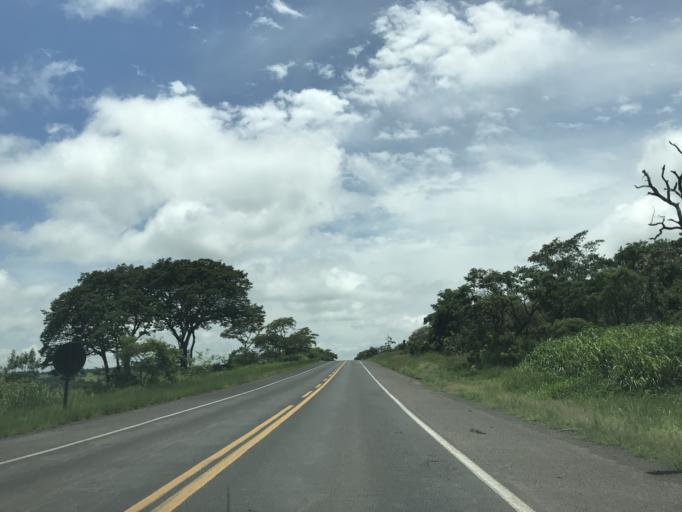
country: BR
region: Minas Gerais
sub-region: Prata
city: Prata
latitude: -19.6283
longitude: -48.9319
